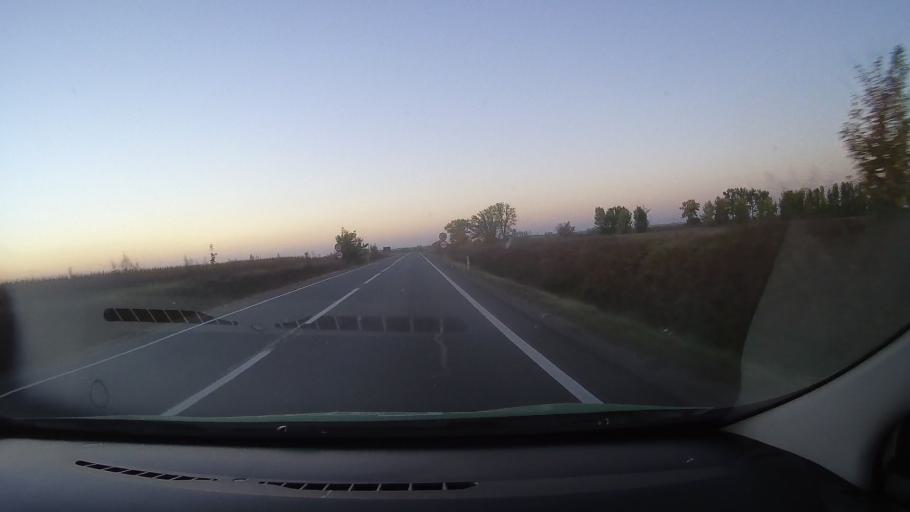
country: RO
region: Bihor
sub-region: Comuna Tarcea
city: Tarcea
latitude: 47.4324
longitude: 22.2057
